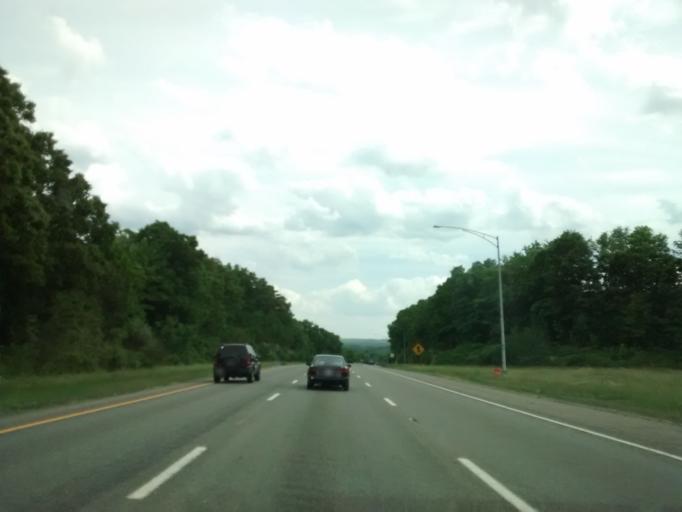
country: US
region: Massachusetts
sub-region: Worcester County
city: Southborough
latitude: 42.2874
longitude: -71.5673
